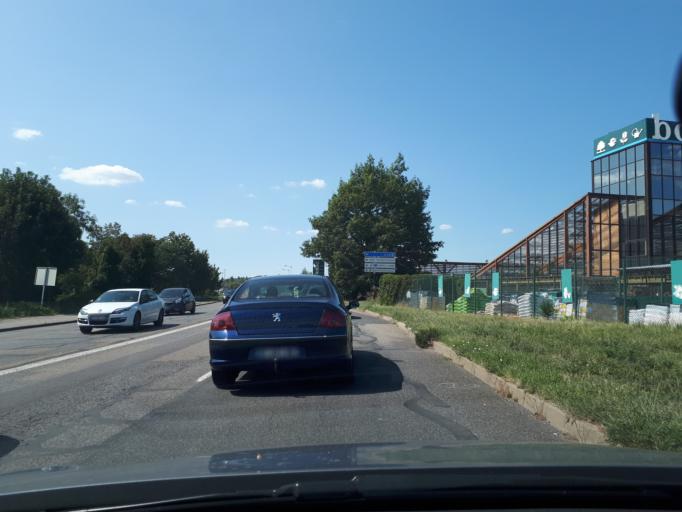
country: FR
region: Rhone-Alpes
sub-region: Departement du Rhone
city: Bron
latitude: 45.7235
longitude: 4.9385
